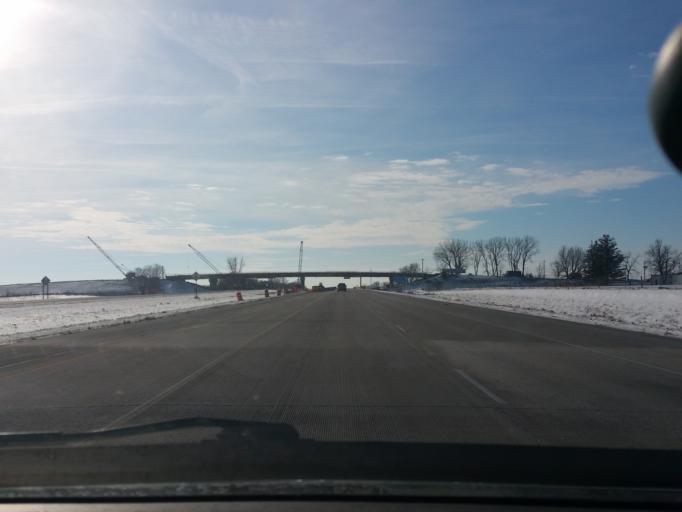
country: US
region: Iowa
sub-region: Polk County
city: West Des Moines
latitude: 41.5081
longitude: -93.7806
